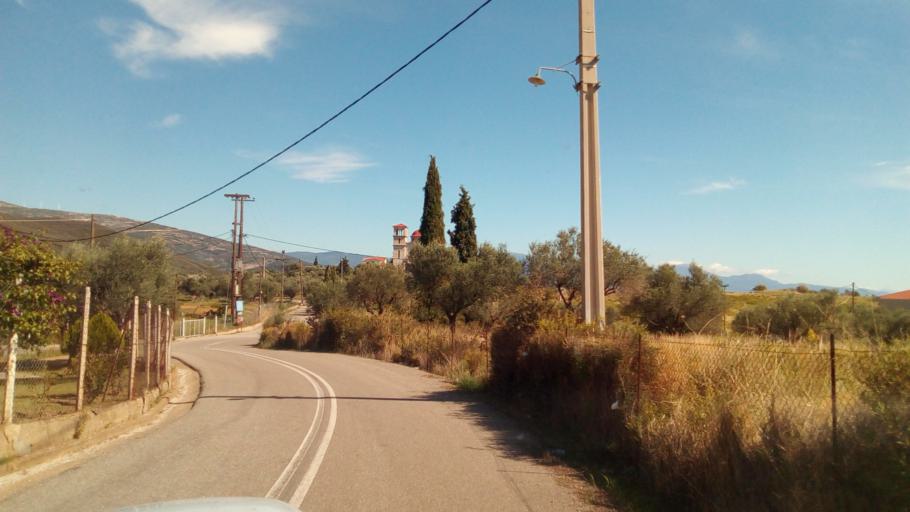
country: GR
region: West Greece
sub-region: Nomos Aitolias kai Akarnanias
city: Antirrio
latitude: 38.3690
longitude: 21.7744
